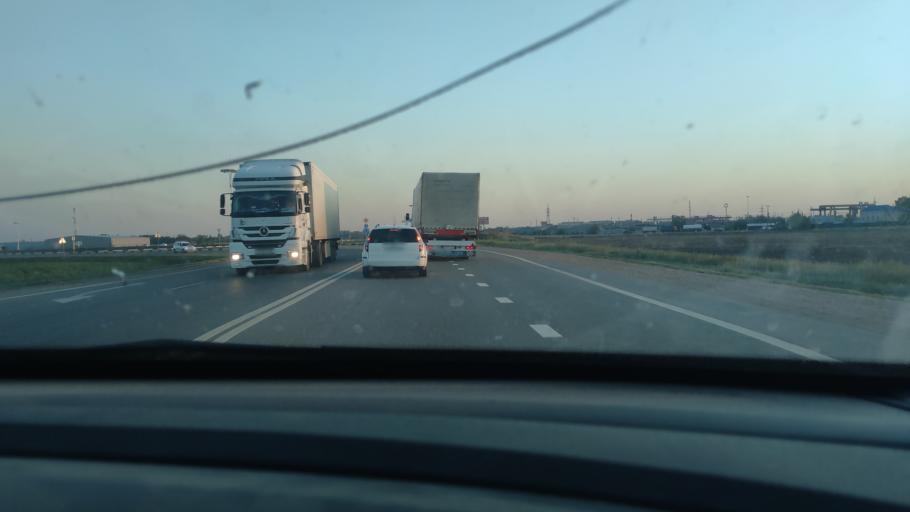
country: RU
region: Krasnodarskiy
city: Timashevsk
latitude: 45.6414
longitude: 38.9699
